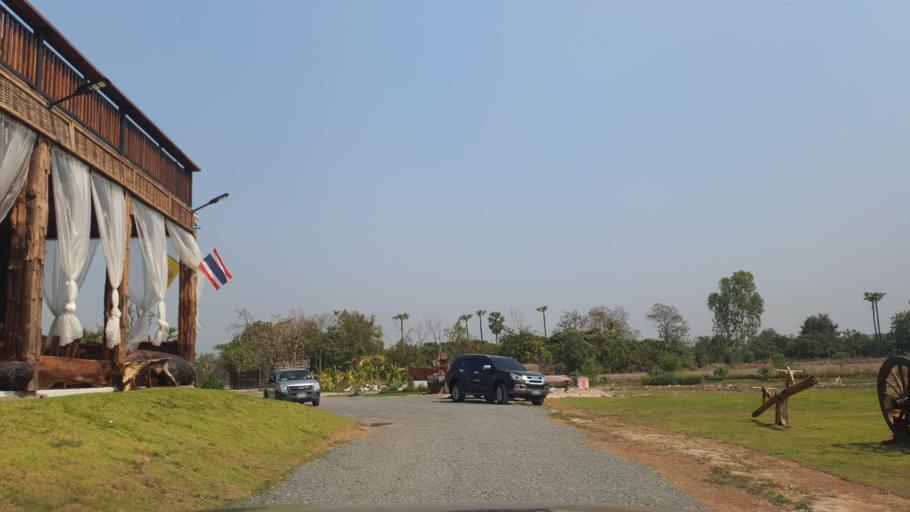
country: TH
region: Lamphun
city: Ban Thi
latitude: 18.6624
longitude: 99.1335
